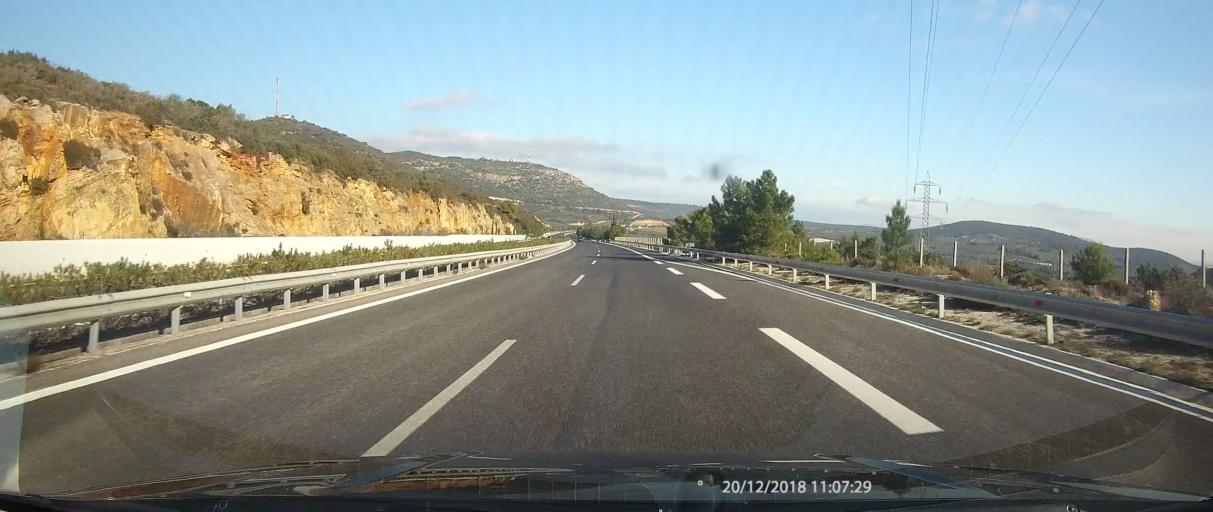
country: GR
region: Peloponnese
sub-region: Nomos Korinthias
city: Nemea
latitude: 37.7884
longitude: 22.7115
